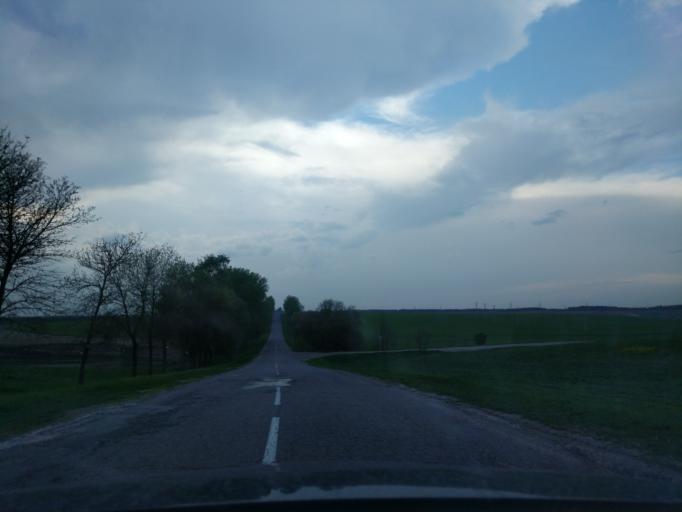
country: BY
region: Minsk
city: Novy Svyerzhan'
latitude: 53.4731
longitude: 26.6373
